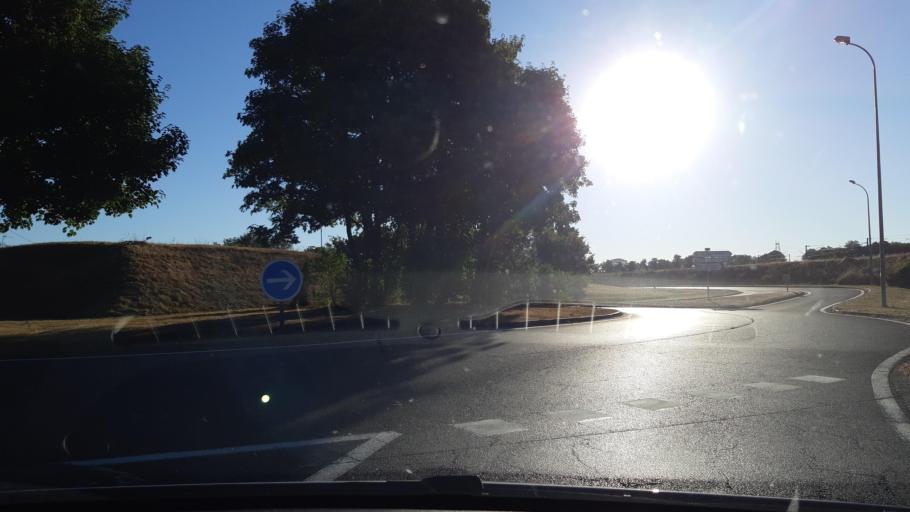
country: FR
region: Poitou-Charentes
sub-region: Departement des Deux-Sevres
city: La Creche
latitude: 46.3693
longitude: -0.2898
